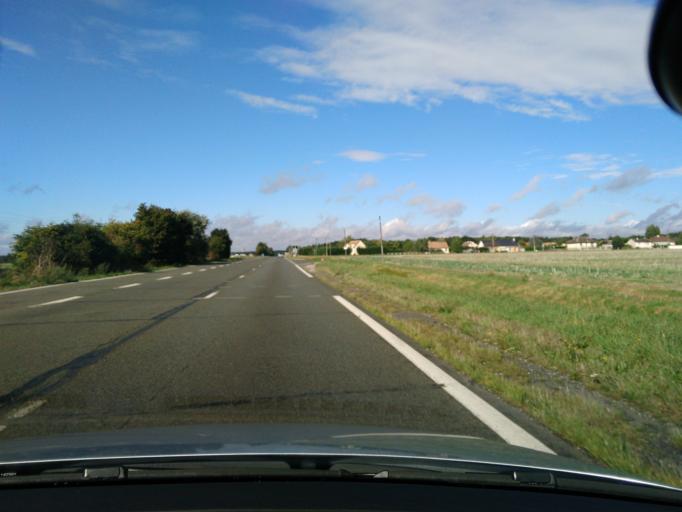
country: FR
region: Centre
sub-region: Departement d'Eure-et-Loir
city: Vert-en-Drouais
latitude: 48.7459
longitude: 1.2808
